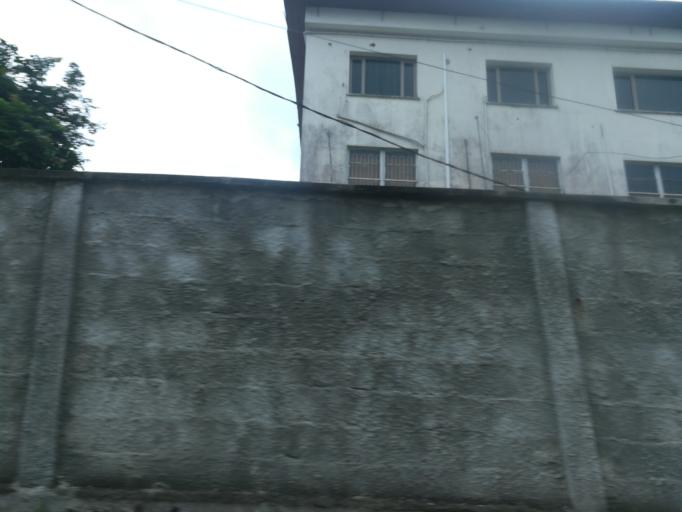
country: NG
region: Lagos
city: Ikoyi
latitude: 6.4427
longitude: 3.4245
